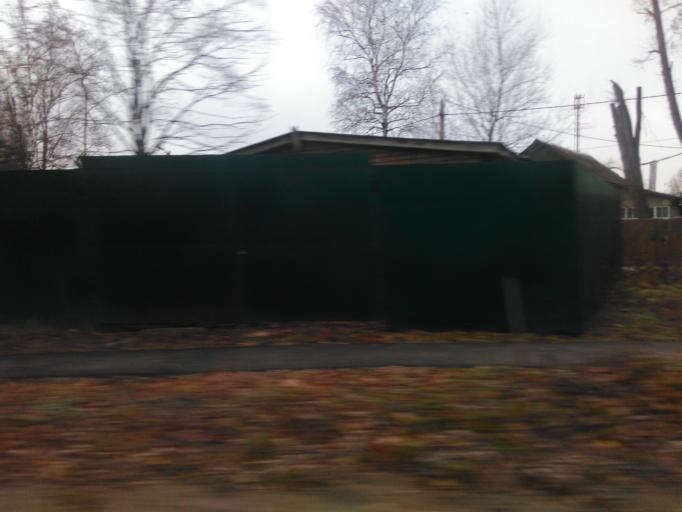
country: RU
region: Moskovskaya
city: Ashukino
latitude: 56.1657
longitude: 37.9452
